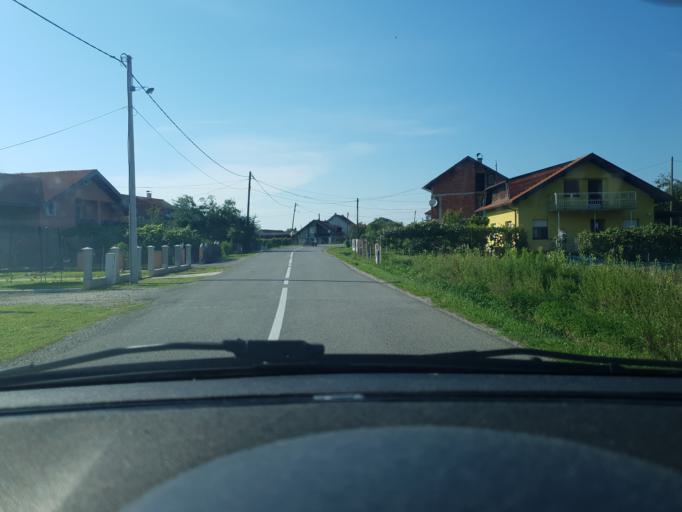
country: HR
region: Zagrebacka
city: Jakovlje
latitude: 45.9331
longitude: 15.8446
